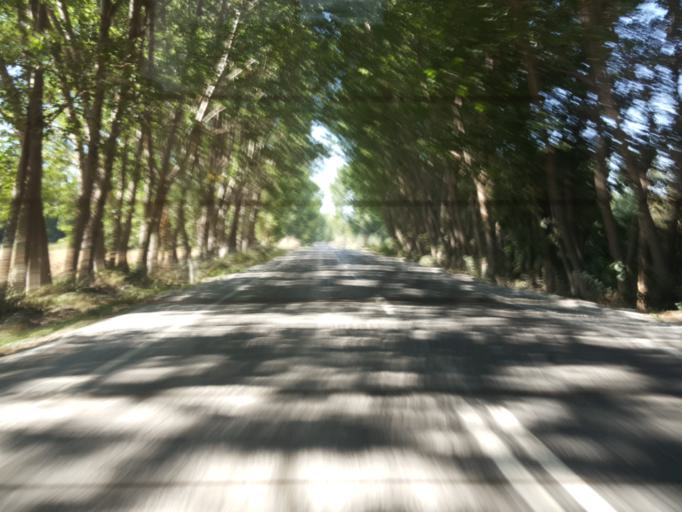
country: TR
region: Tokat
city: Pazar
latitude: 40.2715
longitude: 36.2524
